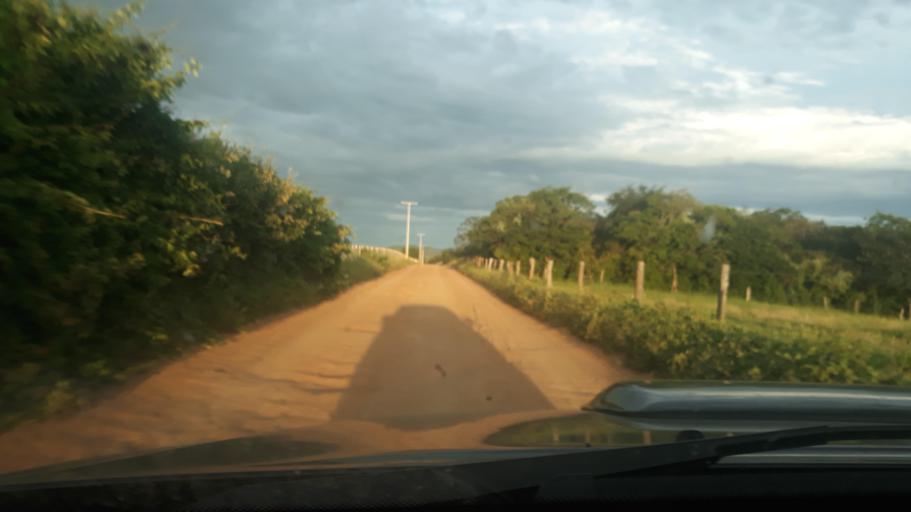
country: BR
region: Bahia
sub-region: Riacho De Santana
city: Riacho de Santana
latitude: -13.9015
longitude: -42.8929
